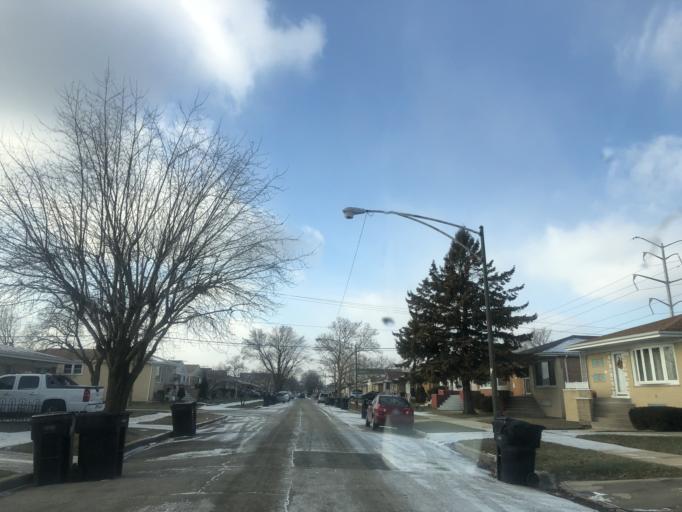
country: US
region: Illinois
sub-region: Cook County
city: Hometown
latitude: 41.7565
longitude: -87.7158
